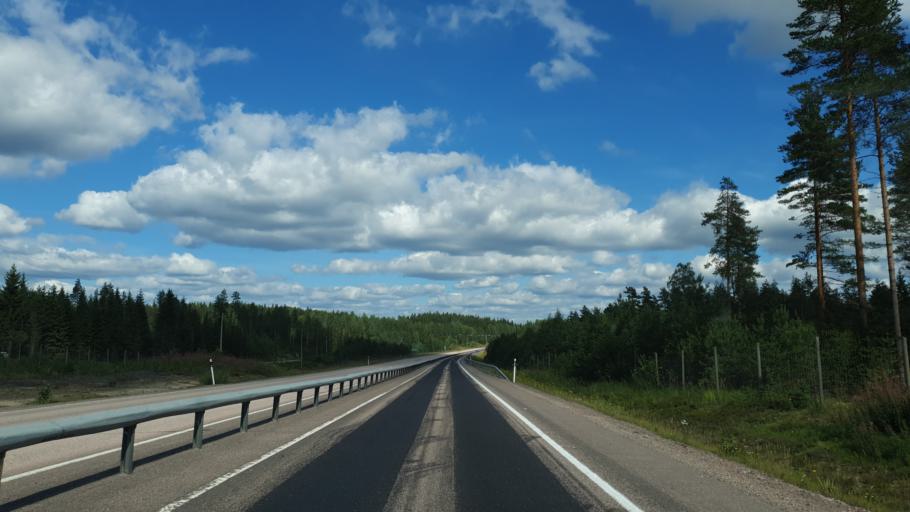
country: FI
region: Central Finland
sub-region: Jaemsae
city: Jaemsae
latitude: 61.7939
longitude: 24.9405
